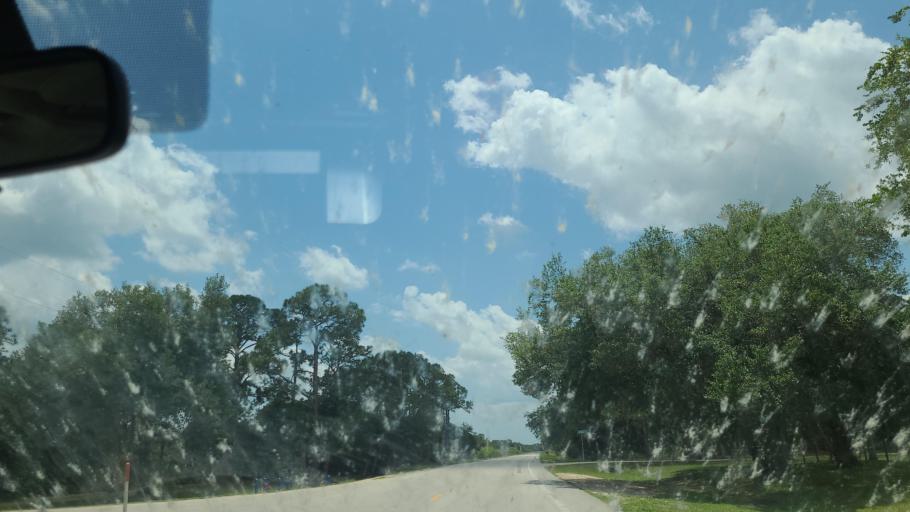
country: US
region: Florida
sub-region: Glades County
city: Buckhead Ridge
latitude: 27.1077
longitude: -81.0691
